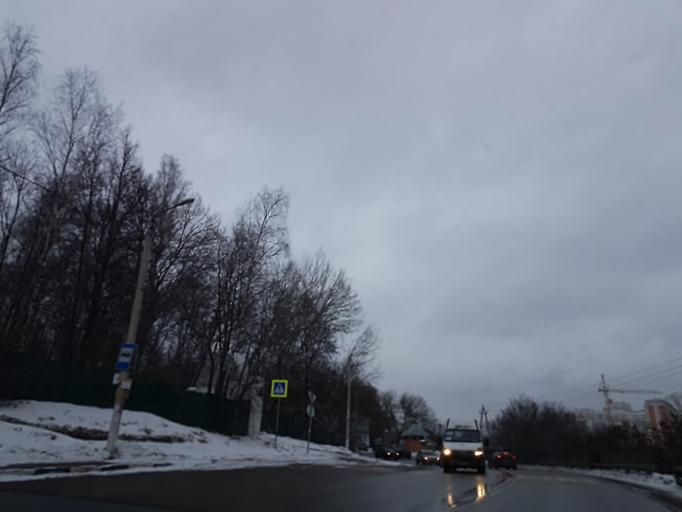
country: RU
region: Moskovskaya
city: Pavshino
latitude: 55.8194
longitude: 37.3582
